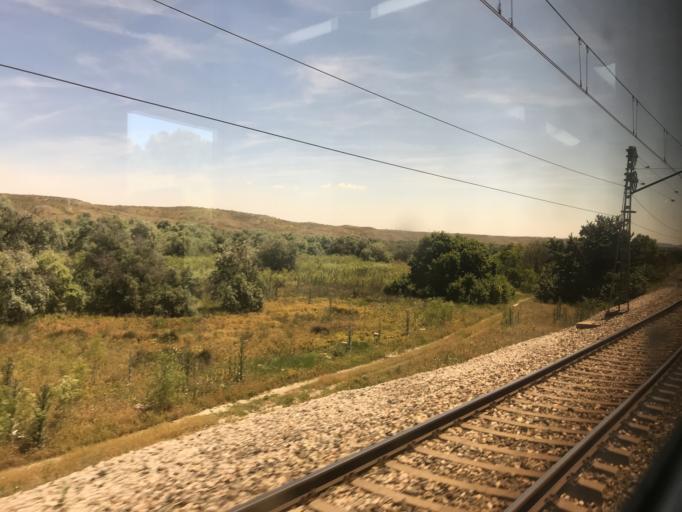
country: ES
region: Madrid
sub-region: Provincia de Madrid
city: Valdemoro
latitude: 40.1885
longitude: -3.6566
